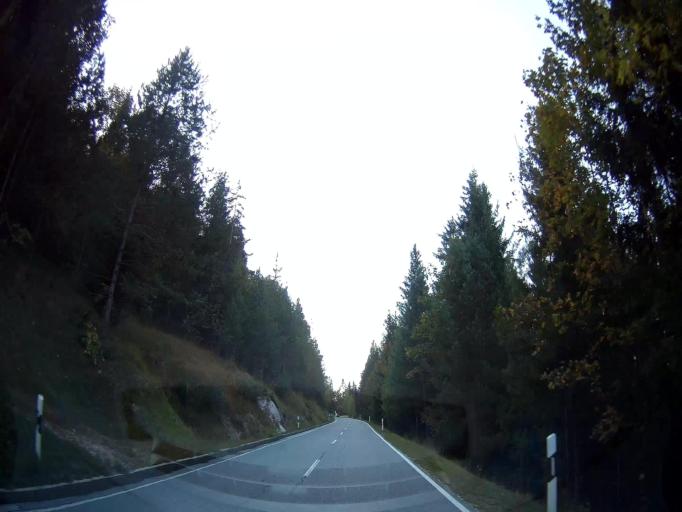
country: DE
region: Bavaria
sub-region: Upper Bavaria
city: Bischofswiesen
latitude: 47.6528
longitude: 12.9491
